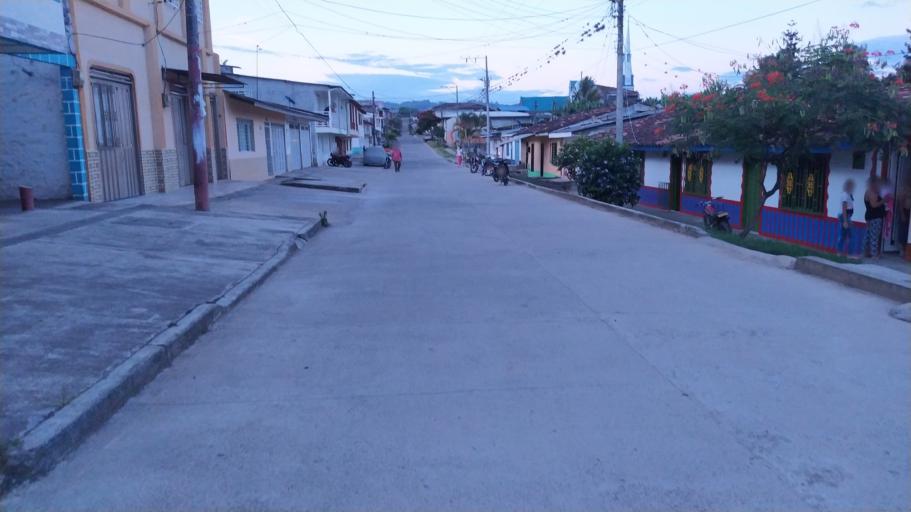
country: CO
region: Valle del Cauca
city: Trujillo
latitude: 4.2115
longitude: -76.3213
